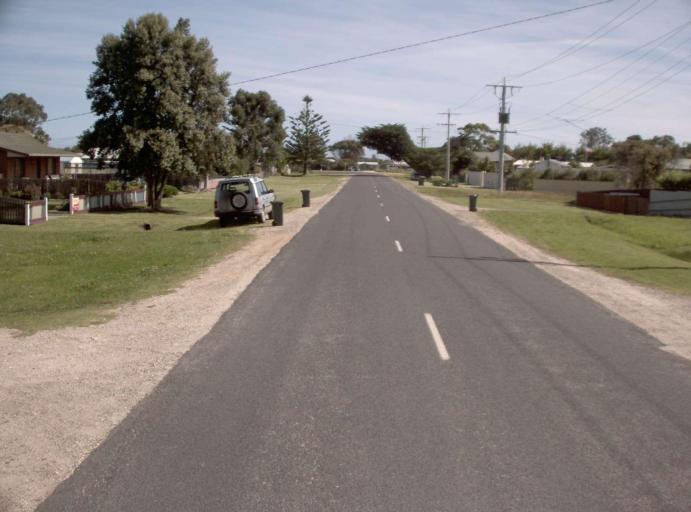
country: AU
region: Victoria
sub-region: Wellington
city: Sale
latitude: -38.3714
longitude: 147.1888
